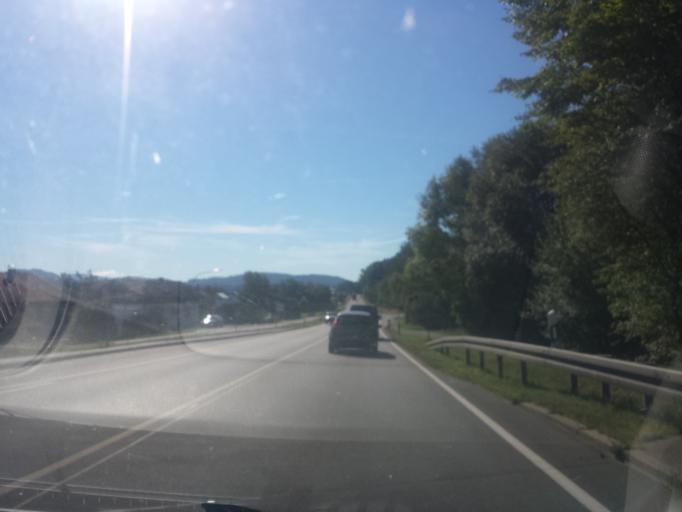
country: DE
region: Bavaria
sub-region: Lower Bavaria
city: Viechtach
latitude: 49.0686
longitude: 12.8914
